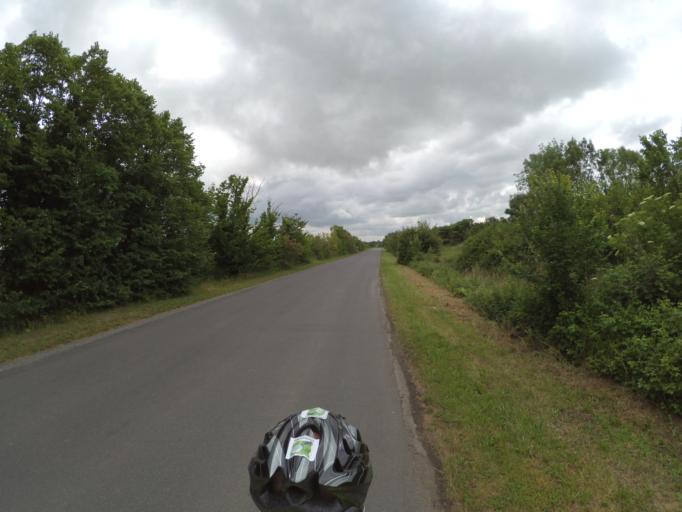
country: FR
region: Poitou-Charentes
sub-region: Departement de la Charente-Maritime
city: Saint-Laurent-de-la-Pree
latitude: 45.9816
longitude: -1.0012
